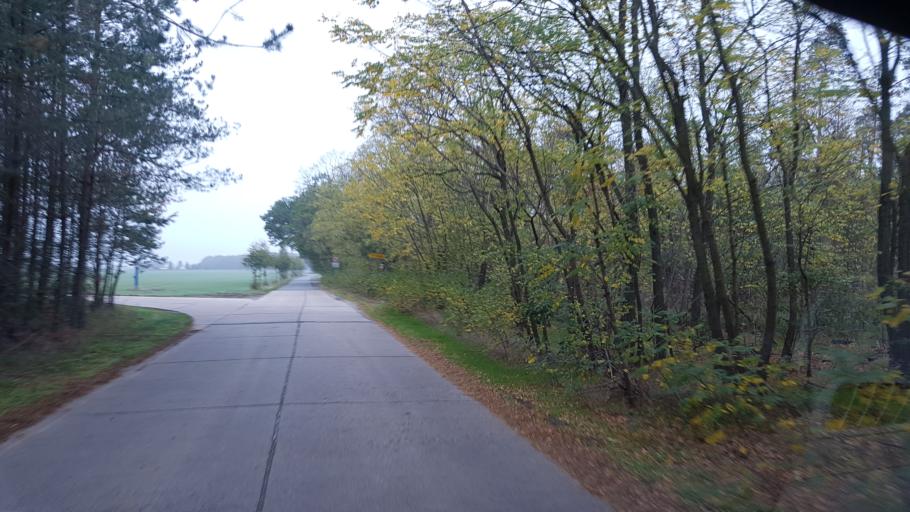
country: DE
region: Brandenburg
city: Sonnewalde
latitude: 51.6714
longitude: 13.6380
